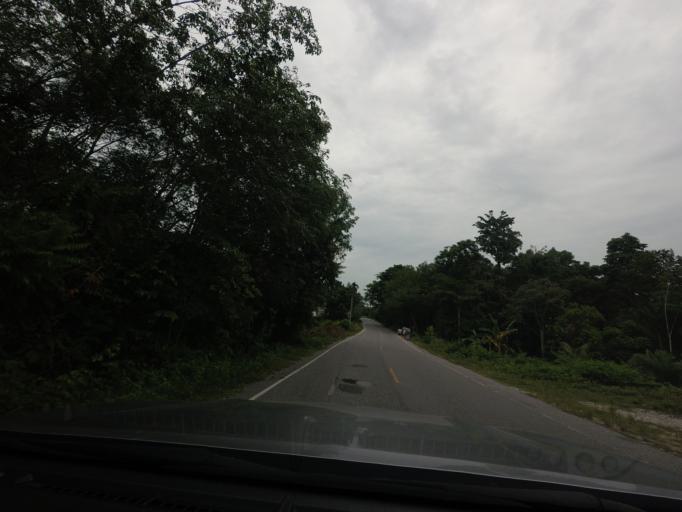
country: TH
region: Narathiwat
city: Rueso
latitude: 6.3520
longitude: 101.4730
